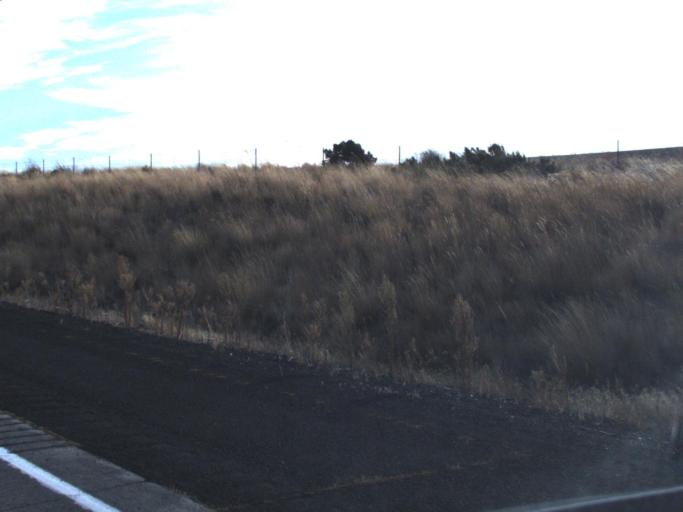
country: US
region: Washington
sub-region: Adams County
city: Ritzville
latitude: 47.0031
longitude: -118.5305
